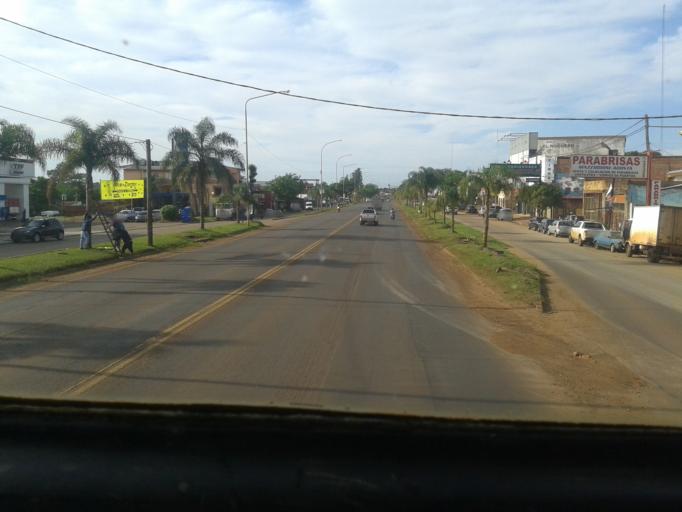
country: AR
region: Misiones
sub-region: Departamento de Capital
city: Posadas
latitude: -27.4086
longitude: -55.9026
